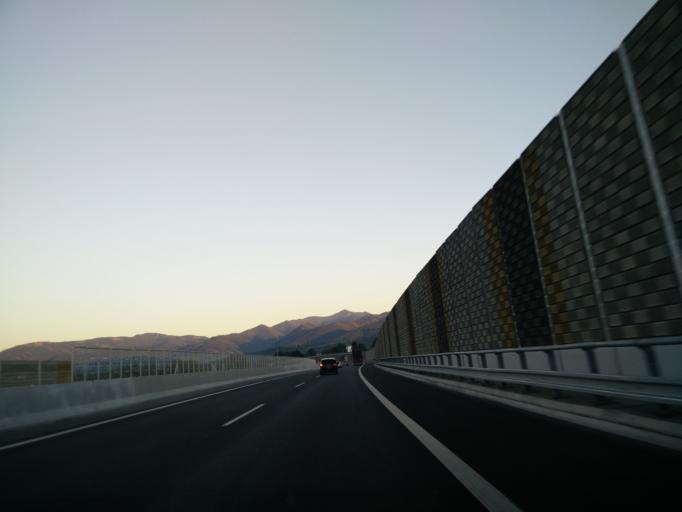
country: SK
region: Zilinsky
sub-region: Okres Zilina
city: Vrutky
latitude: 49.1069
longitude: 18.9809
